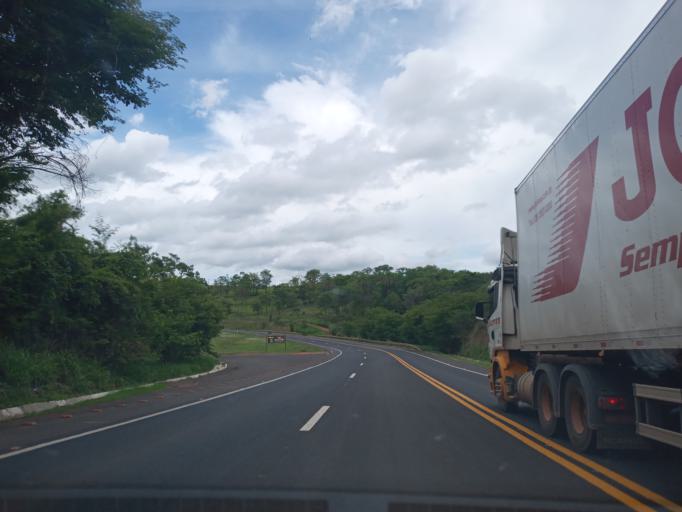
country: BR
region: Minas Gerais
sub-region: Uberaba
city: Uberaba
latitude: -19.2824
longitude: -47.6239
